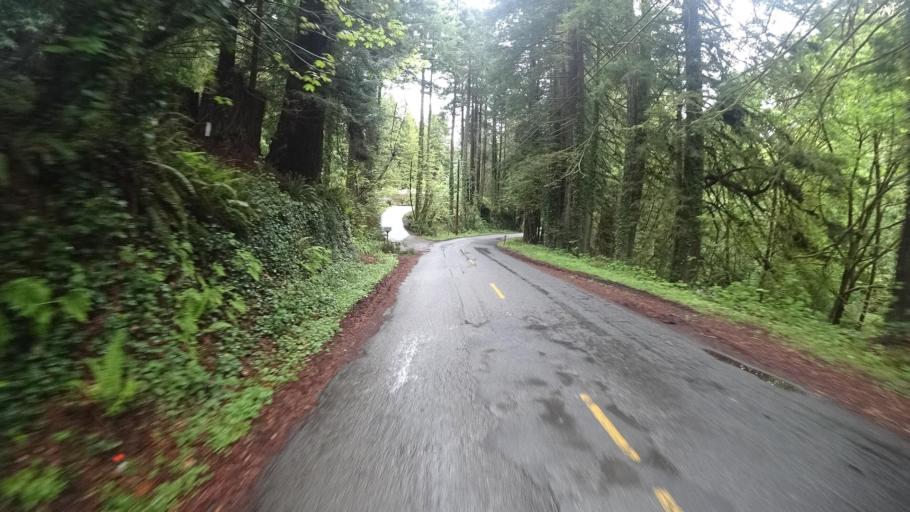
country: US
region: California
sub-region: Humboldt County
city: Bayside
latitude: 40.8276
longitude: -124.0382
